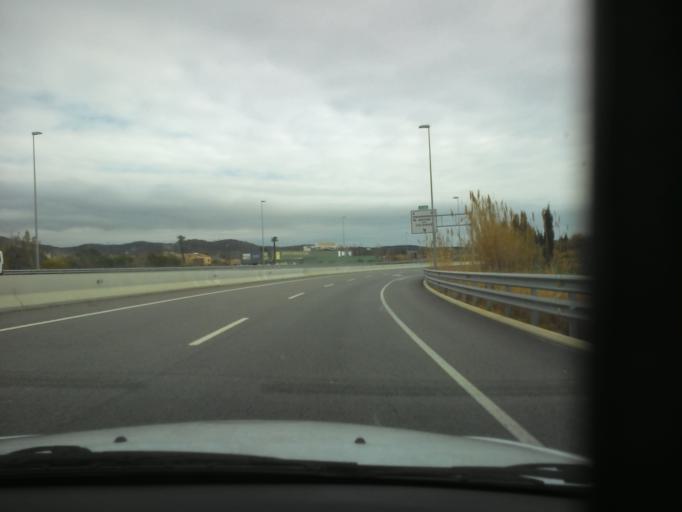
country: ES
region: Catalonia
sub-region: Provincia de Girona
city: Calonge
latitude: 41.8570
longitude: 3.0745
